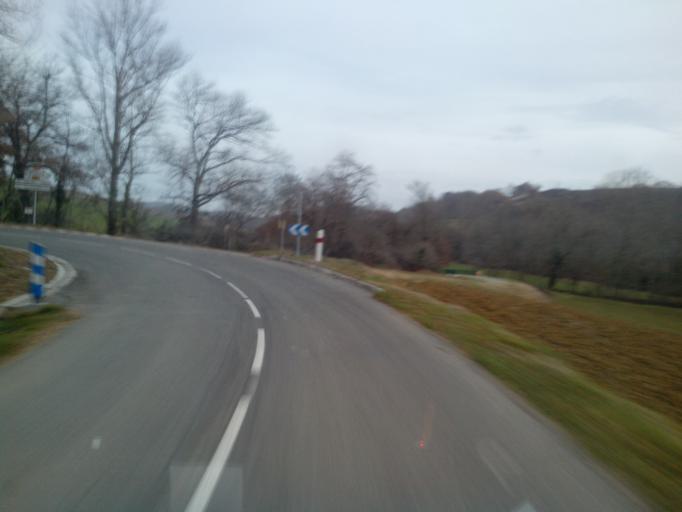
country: FR
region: Midi-Pyrenees
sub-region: Departement de l'Ariege
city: Mazeres
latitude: 43.2491
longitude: 1.7307
